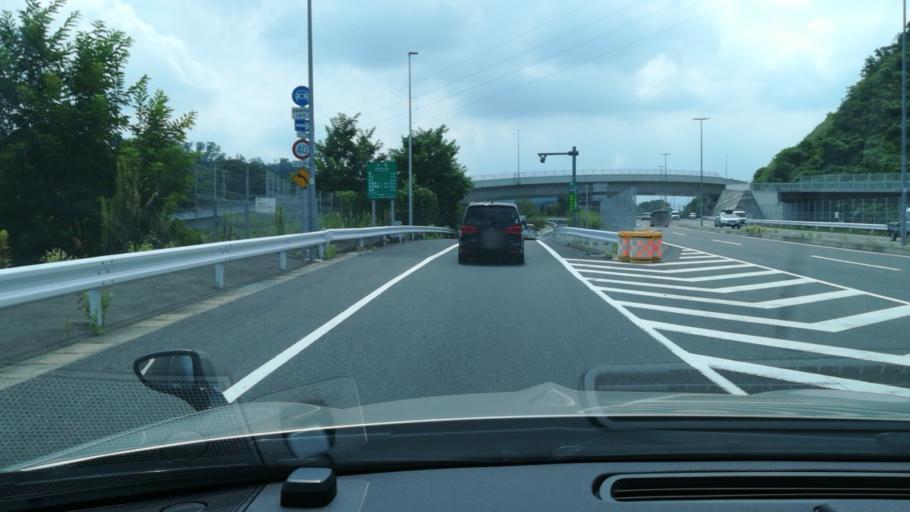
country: JP
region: Tokyo
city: Hachioji
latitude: 35.5814
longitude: 139.2900
